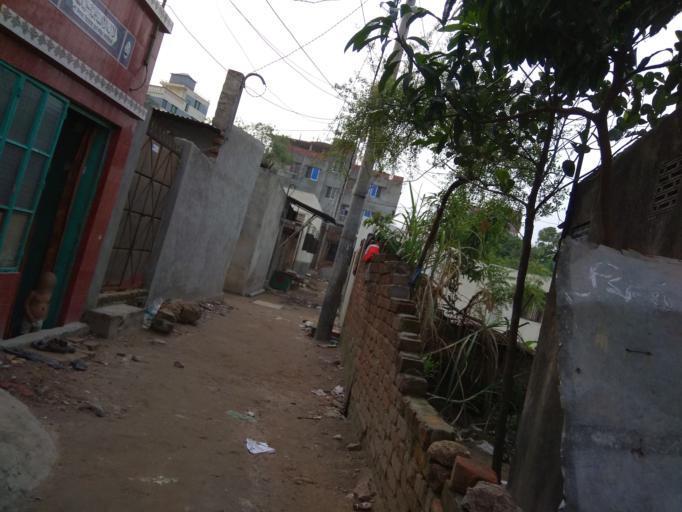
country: BD
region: Dhaka
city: Tungi
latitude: 23.8127
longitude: 90.3830
